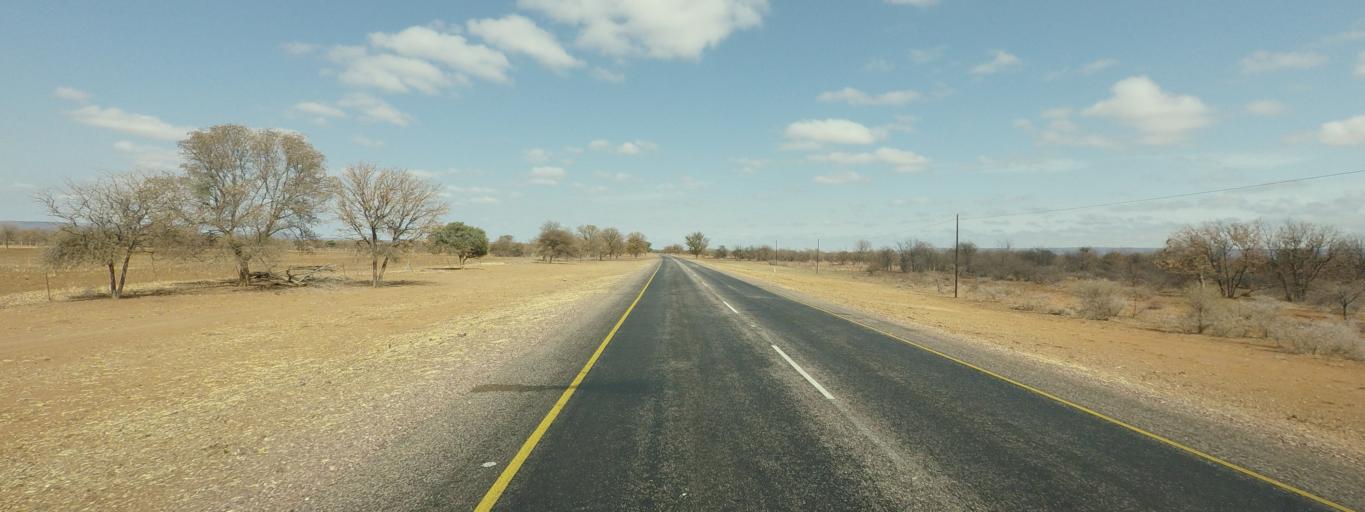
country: BW
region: Central
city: Ramokgonami
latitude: -22.7906
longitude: 27.4521
